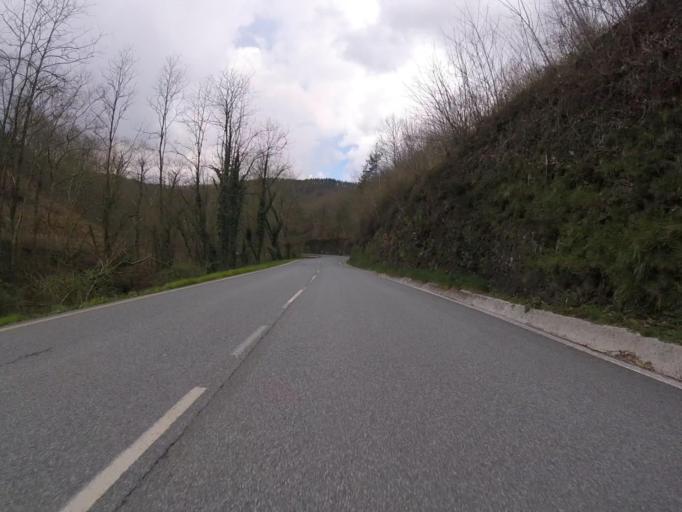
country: ES
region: Navarre
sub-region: Provincia de Navarra
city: Etxalar
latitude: 43.2369
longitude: -1.6569
